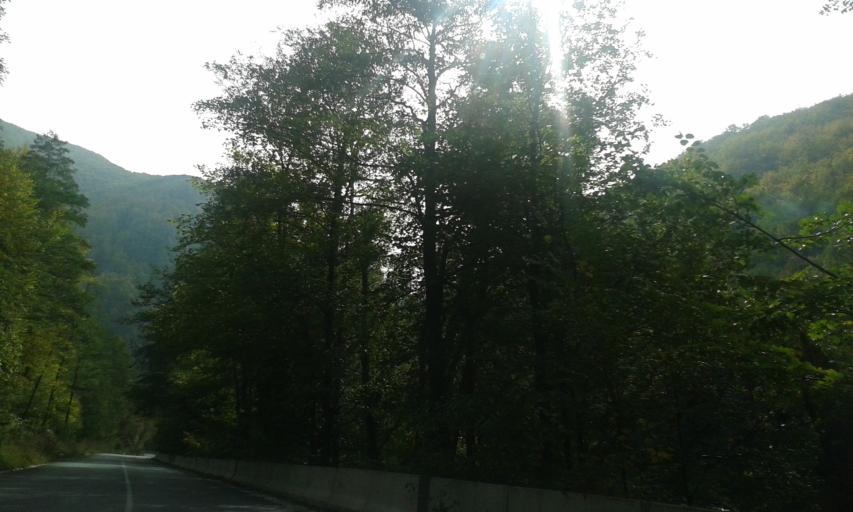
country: RO
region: Gorj
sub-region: Comuna Bumbesti-Jiu
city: Bumbesti-Jiu
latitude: 45.2436
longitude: 23.3899
